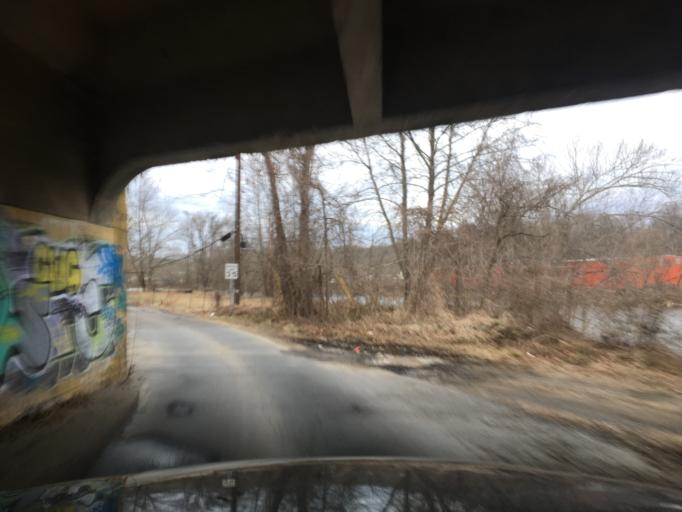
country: US
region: North Carolina
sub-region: Buncombe County
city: Asheville
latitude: 35.5933
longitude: -82.5737
